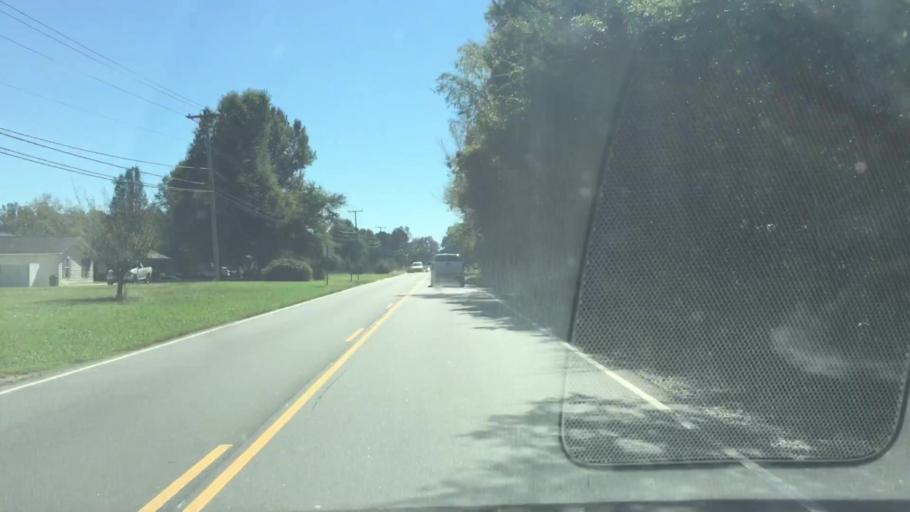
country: US
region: North Carolina
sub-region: Rowan County
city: Enochville
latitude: 35.4494
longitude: -80.7309
